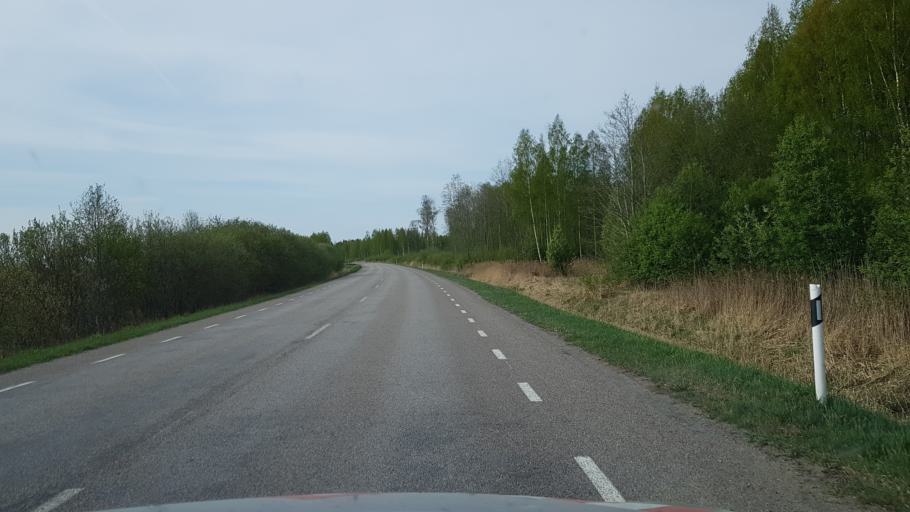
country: EE
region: Paernumaa
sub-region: Audru vald
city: Audru
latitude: 58.3889
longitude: 24.2747
